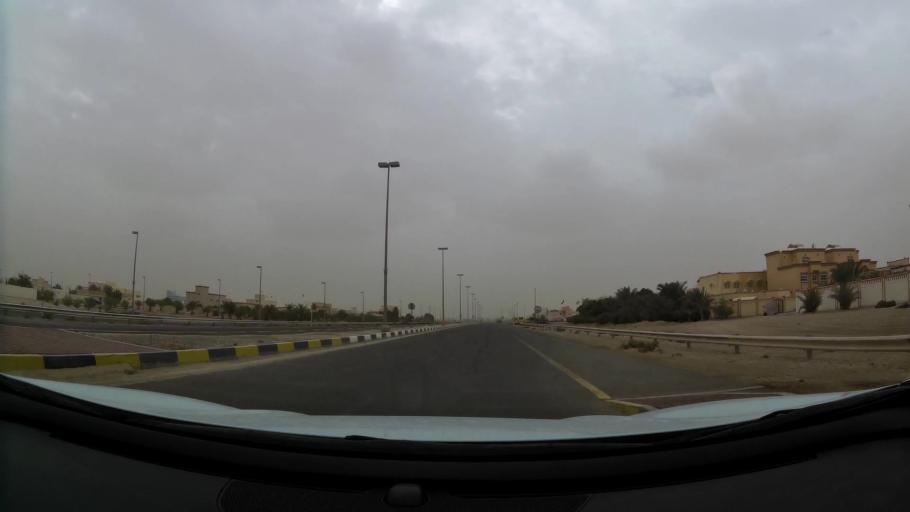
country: AE
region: Abu Dhabi
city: Abu Dhabi
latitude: 24.4247
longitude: 54.7427
